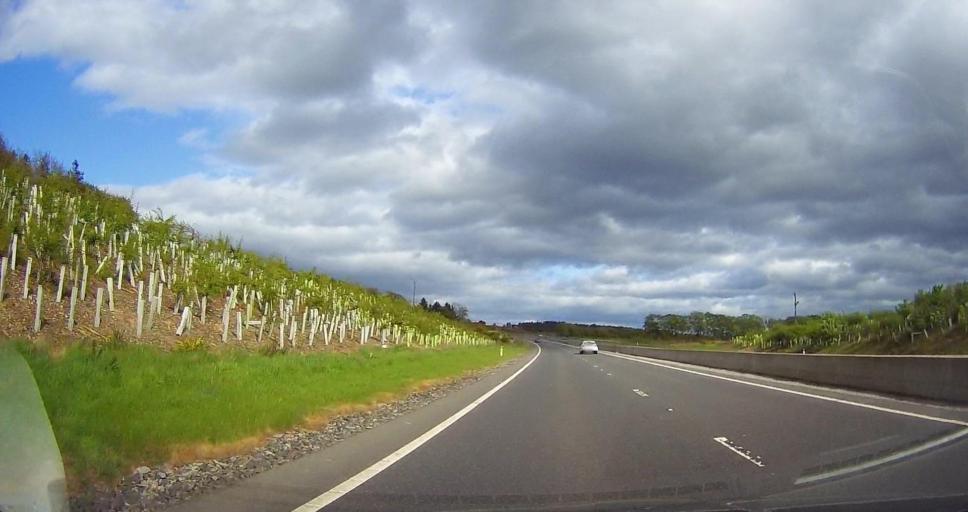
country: GB
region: Scotland
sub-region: Aberdeen City
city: Cults
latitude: 57.0781
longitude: -2.2077
